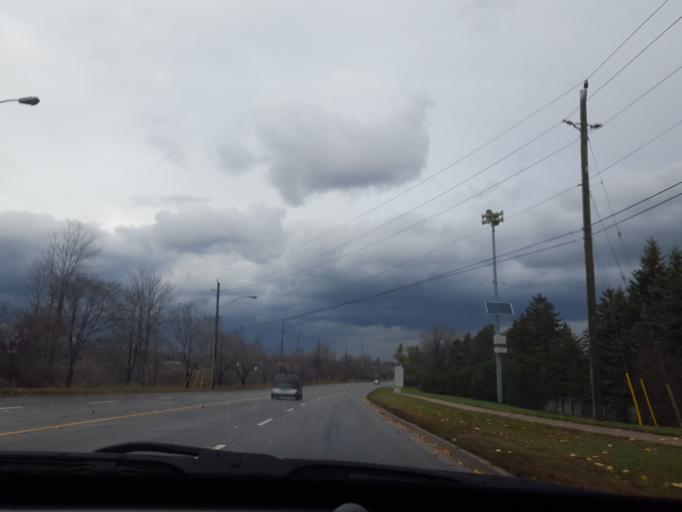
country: CA
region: Ontario
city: Ajax
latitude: 43.8168
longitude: -79.1110
